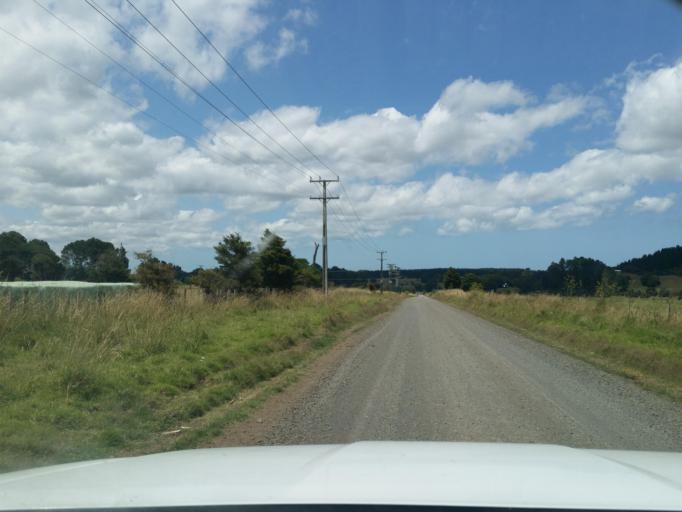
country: NZ
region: Northland
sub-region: Kaipara District
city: Dargaville
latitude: -35.7965
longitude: 173.7318
